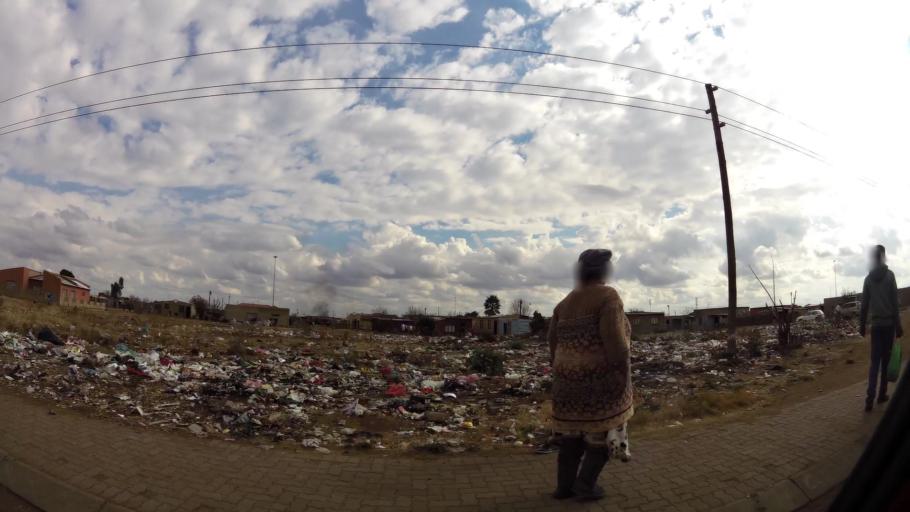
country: ZA
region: Gauteng
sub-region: Sedibeng District Municipality
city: Vanderbijlpark
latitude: -26.6975
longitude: 27.7909
